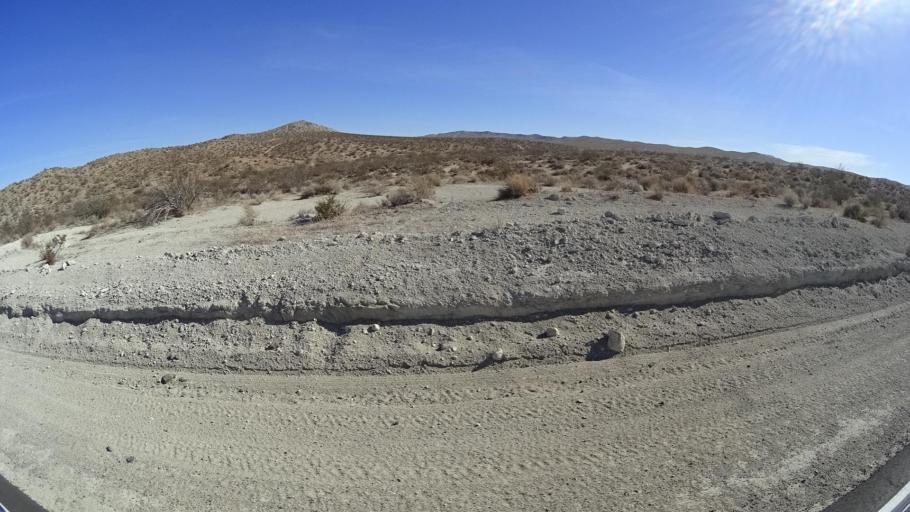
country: US
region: California
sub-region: Kern County
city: Ridgecrest
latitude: 35.4977
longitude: -117.6258
